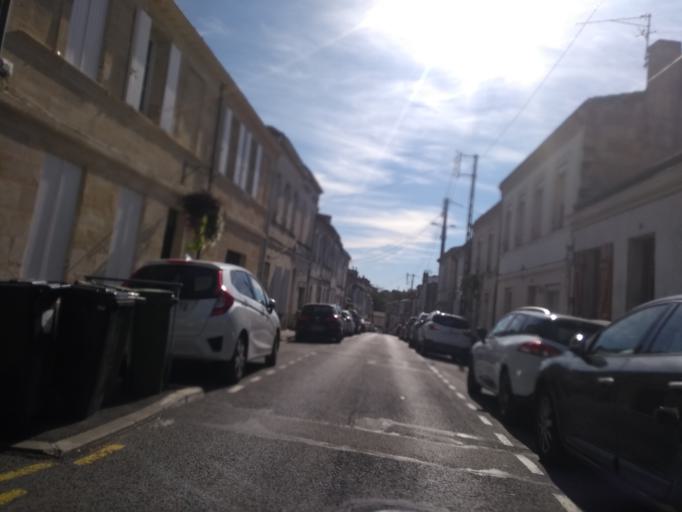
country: FR
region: Aquitaine
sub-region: Departement de la Gironde
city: Lormont
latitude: 44.8790
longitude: -0.5253
